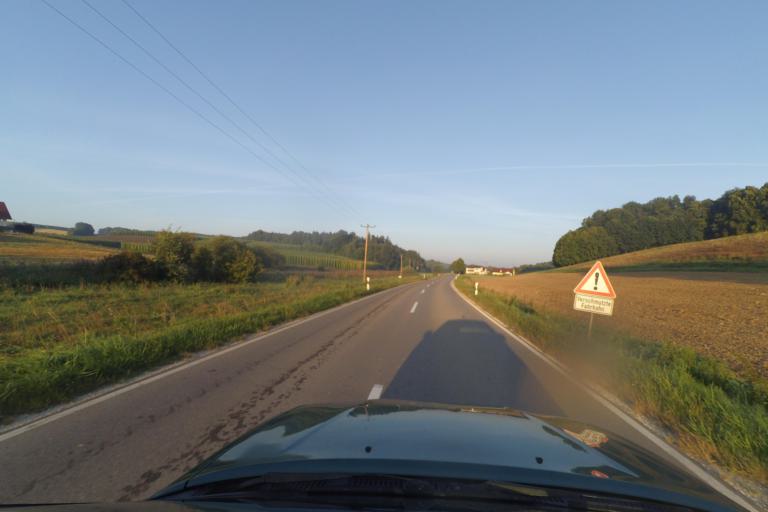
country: DE
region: Bavaria
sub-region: Lower Bavaria
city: Aiglsbach
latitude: 48.6712
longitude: 11.6974
